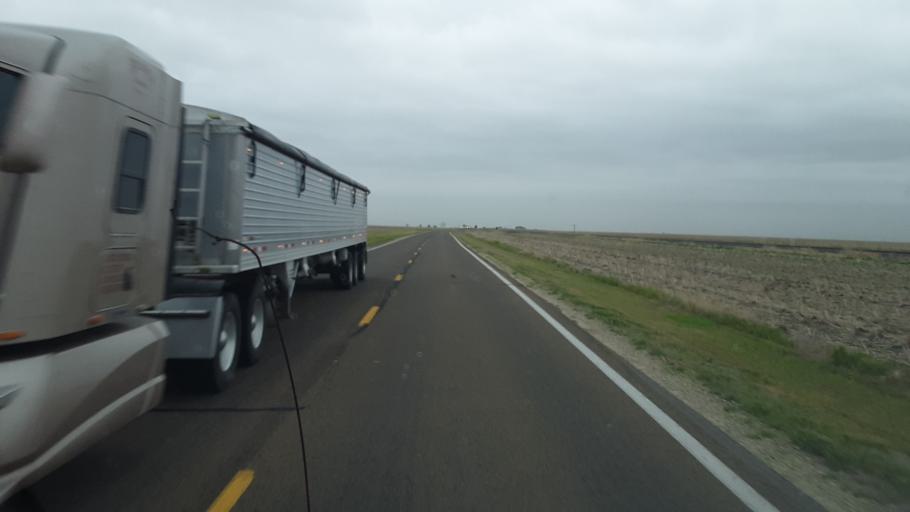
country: US
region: Kansas
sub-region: Logan County
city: Oakley
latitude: 39.0991
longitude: -101.0849
